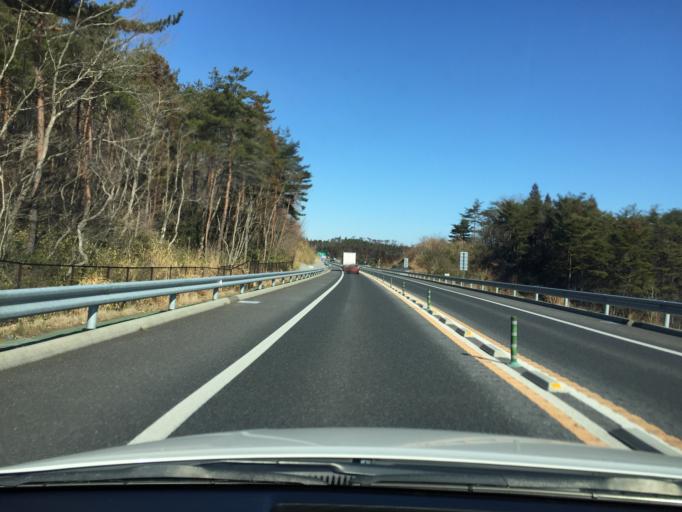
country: JP
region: Fukushima
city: Namie
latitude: 37.7029
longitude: 140.9232
